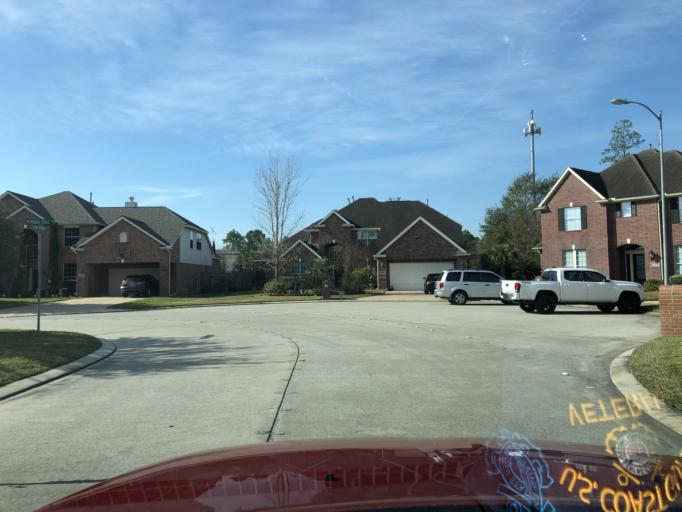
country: US
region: Texas
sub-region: Harris County
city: Tomball
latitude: 30.0258
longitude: -95.5622
